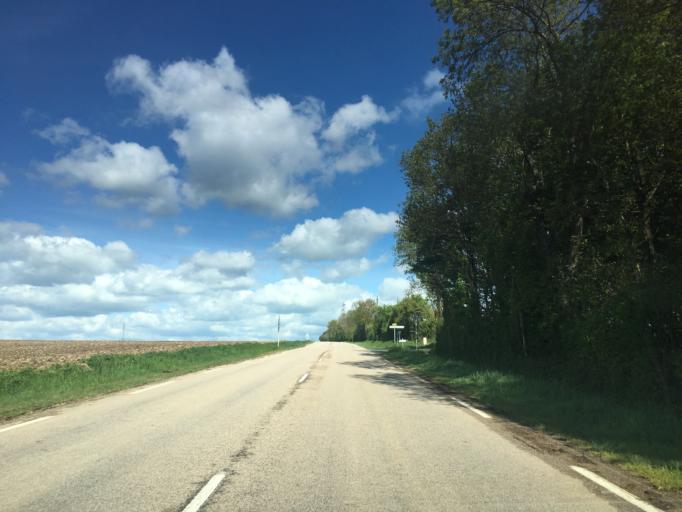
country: FR
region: Lower Normandy
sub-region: Departement de l'Orne
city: Rai
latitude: 48.8048
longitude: 0.5850
